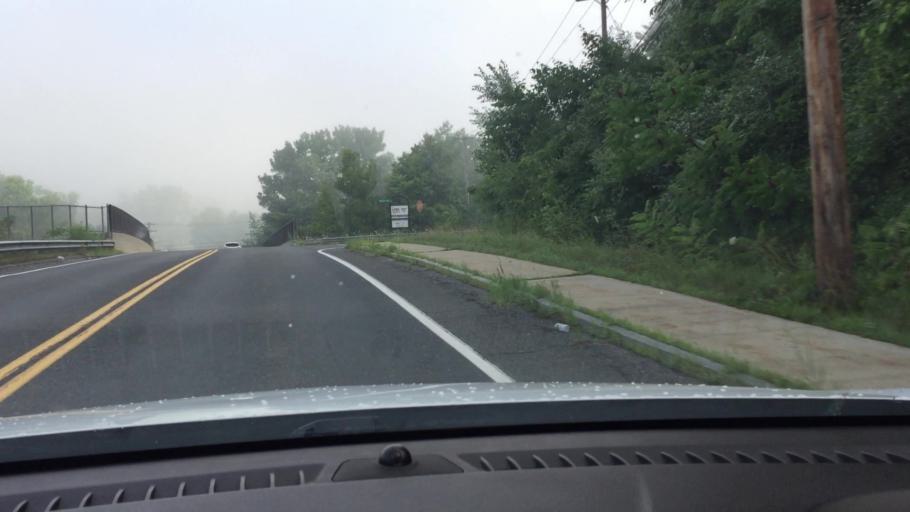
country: US
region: Massachusetts
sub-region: Berkshire County
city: Lee
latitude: 42.3312
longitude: -73.2453
